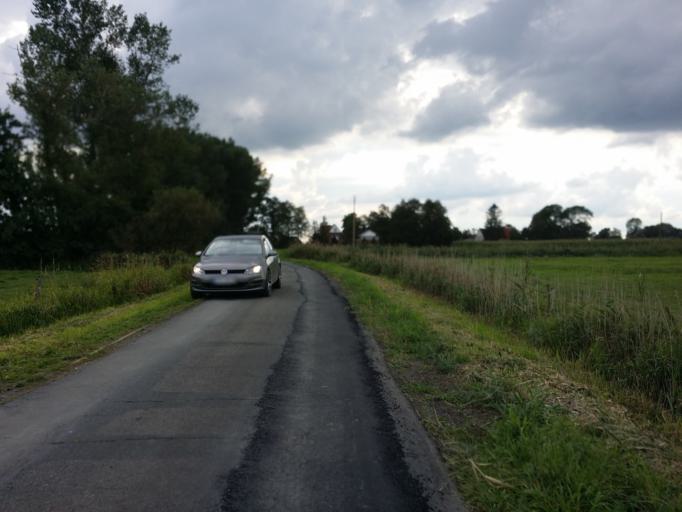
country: DE
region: Lower Saxony
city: Oederquart
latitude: 53.7737
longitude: 9.2169
